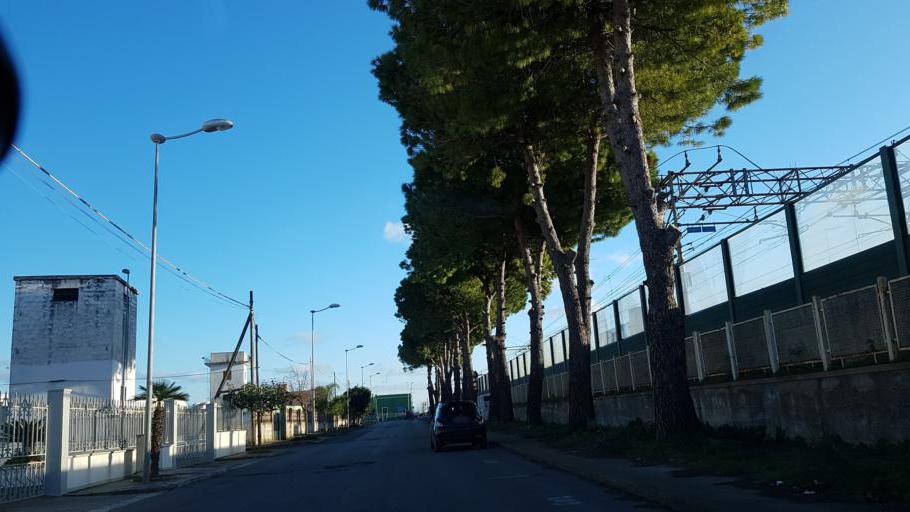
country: IT
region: Apulia
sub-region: Provincia di Lecce
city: Squinzano
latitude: 40.4352
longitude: 18.0506
